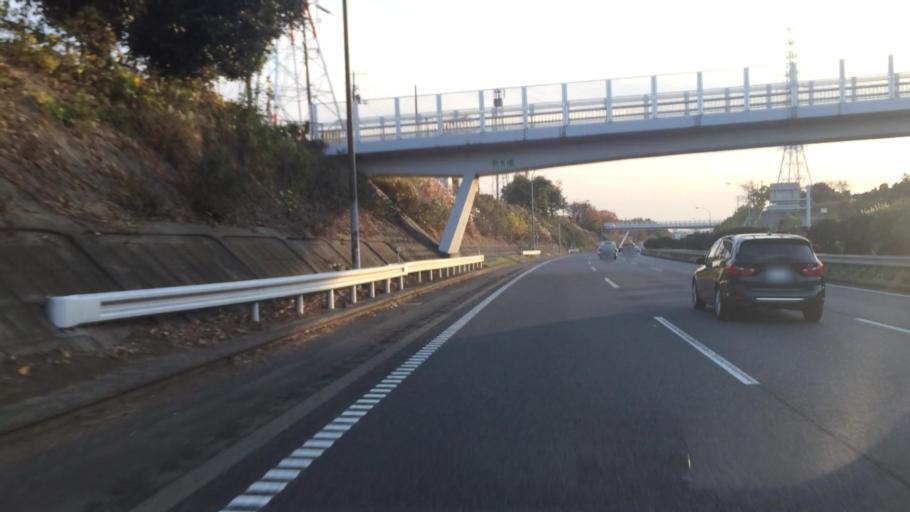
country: JP
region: Kanagawa
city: Yokohama
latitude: 35.5356
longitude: 139.6012
